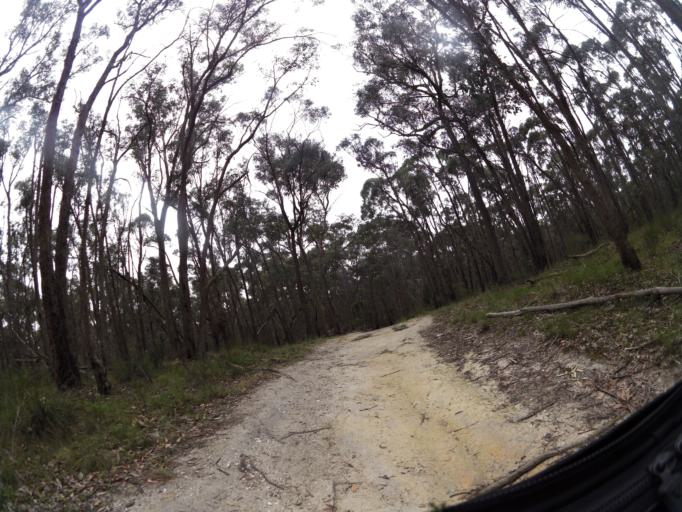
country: AU
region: Victoria
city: Brown Hill
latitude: -37.4510
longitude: 143.9087
